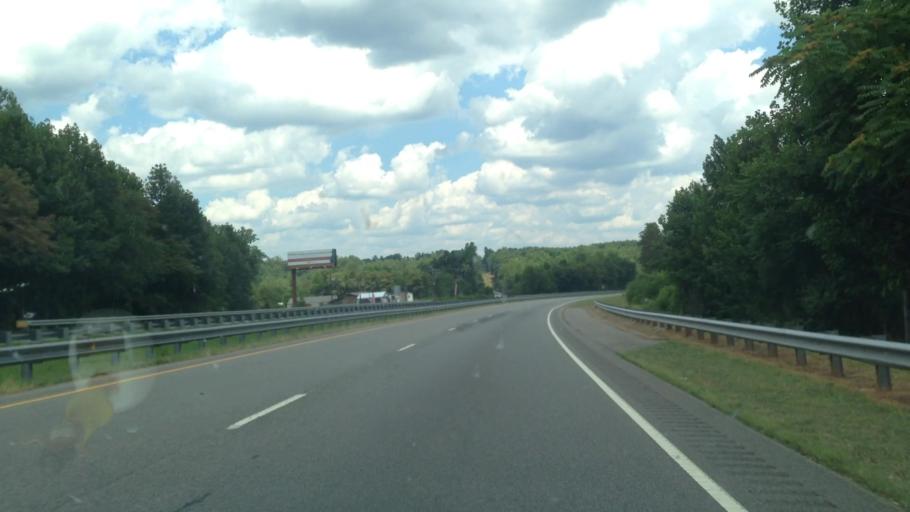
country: US
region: North Carolina
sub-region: Rockingham County
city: Stoneville
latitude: 36.5235
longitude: -79.9174
